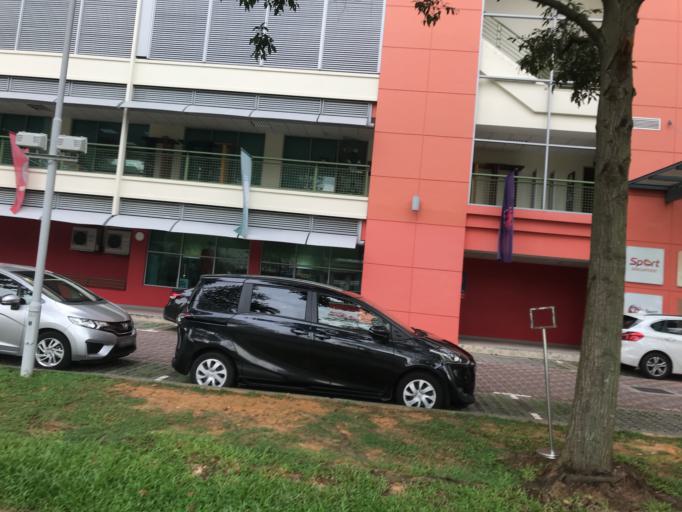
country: SG
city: Singapore
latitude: 1.3096
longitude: 103.8598
